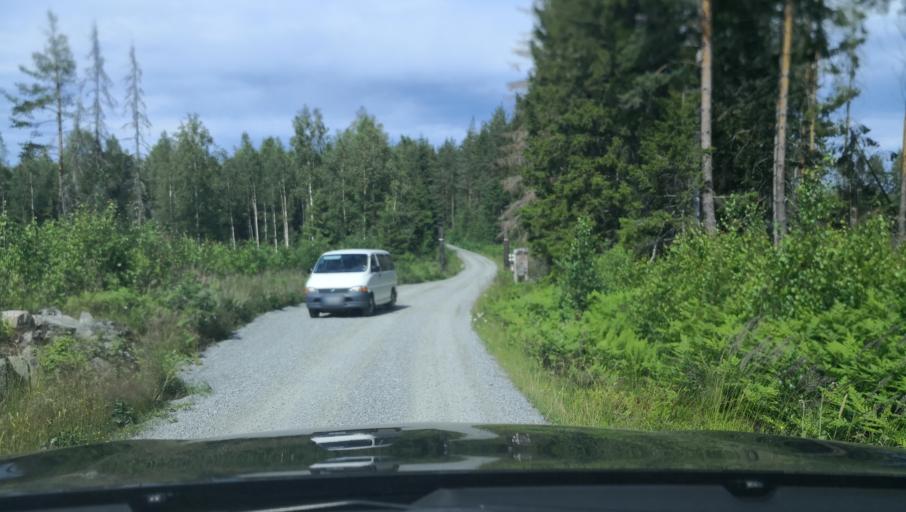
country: SE
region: Vaestmanland
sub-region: Surahammars Kommun
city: Ramnas
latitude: 59.9366
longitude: 16.1935
